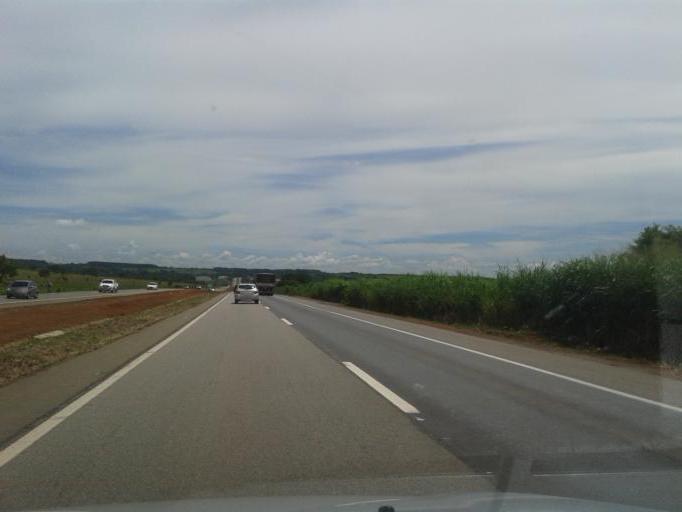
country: BR
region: Goias
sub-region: Hidrolandia
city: Hidrolandia
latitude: -17.0388
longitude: -49.2245
